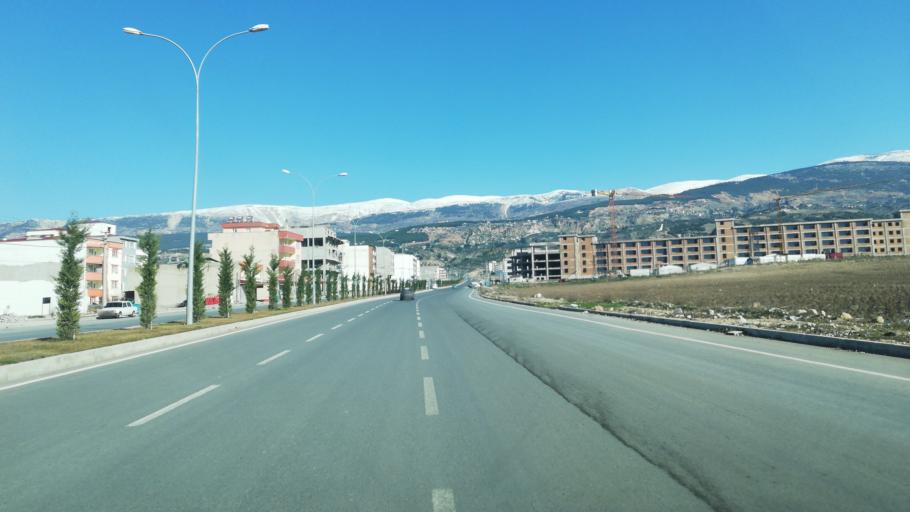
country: TR
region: Kahramanmaras
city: Kahramanmaras
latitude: 37.5727
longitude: 36.9746
